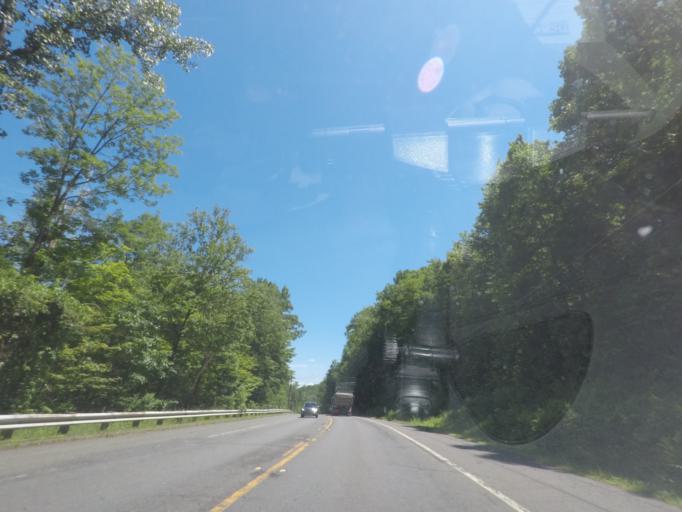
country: US
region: Massachusetts
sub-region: Hampden County
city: Westfield
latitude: 42.1611
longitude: -72.8267
